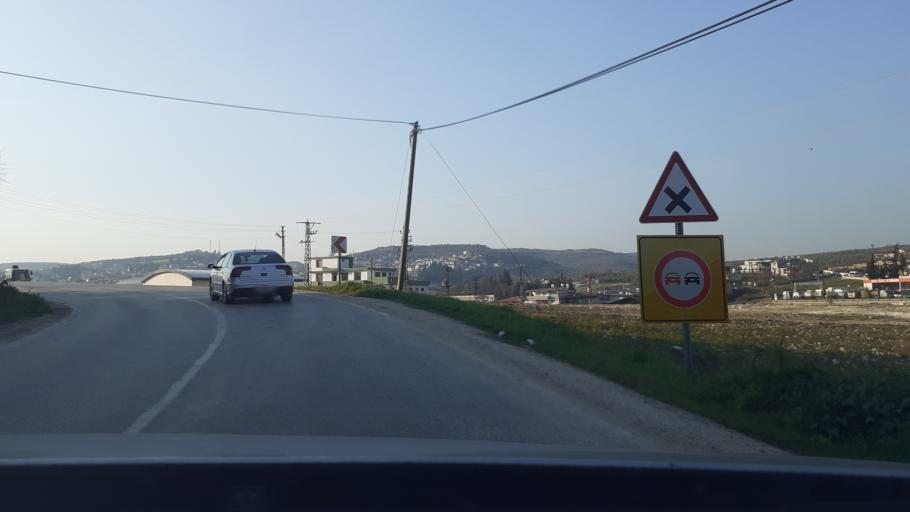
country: TR
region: Hatay
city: Fatikli
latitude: 36.1115
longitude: 36.2648
